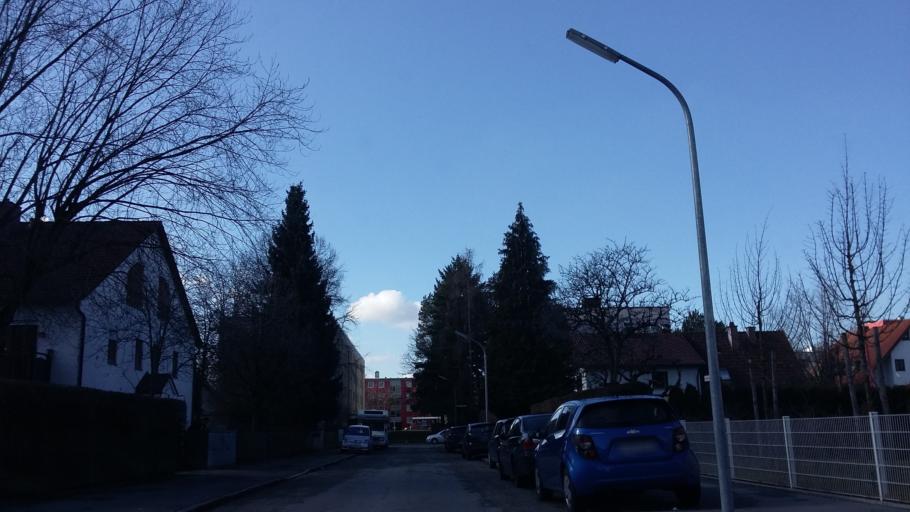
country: DE
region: Bavaria
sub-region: Upper Bavaria
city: Grafelfing
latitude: 48.1491
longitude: 11.4160
